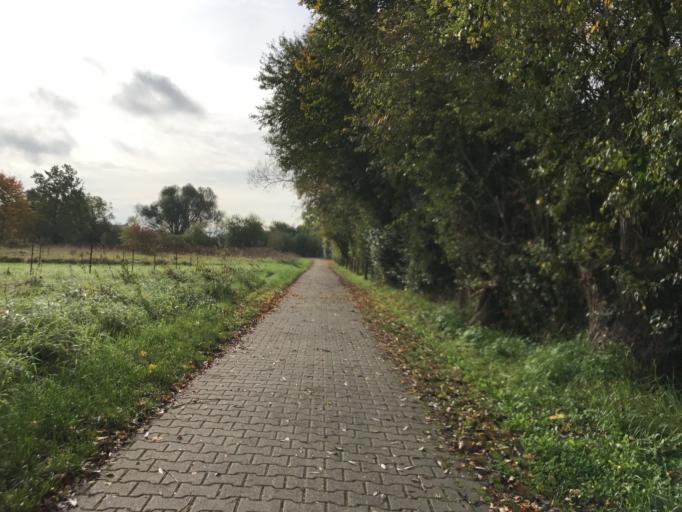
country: DE
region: Rheinland-Pfalz
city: Schwabenheim
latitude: 49.9319
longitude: 8.0846
